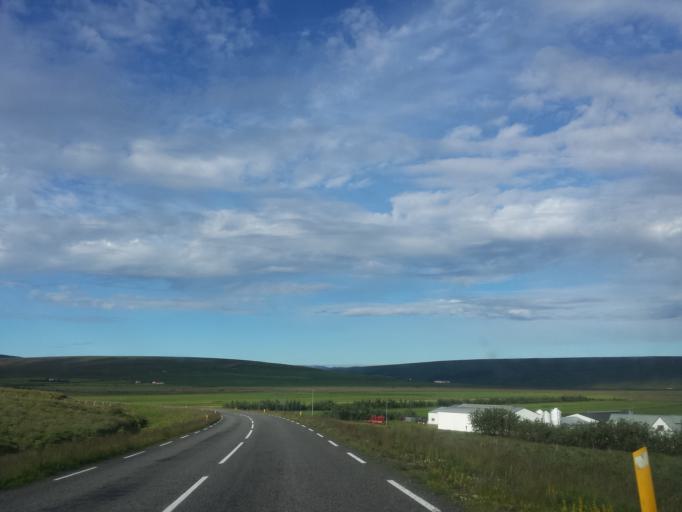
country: IS
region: Northeast
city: Laugar
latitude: 65.7121
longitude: -17.6068
